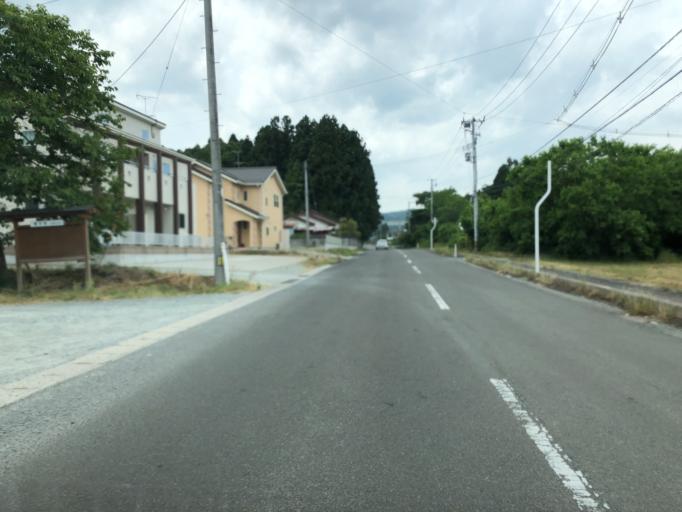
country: JP
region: Miyagi
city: Marumori
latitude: 37.8210
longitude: 140.8837
